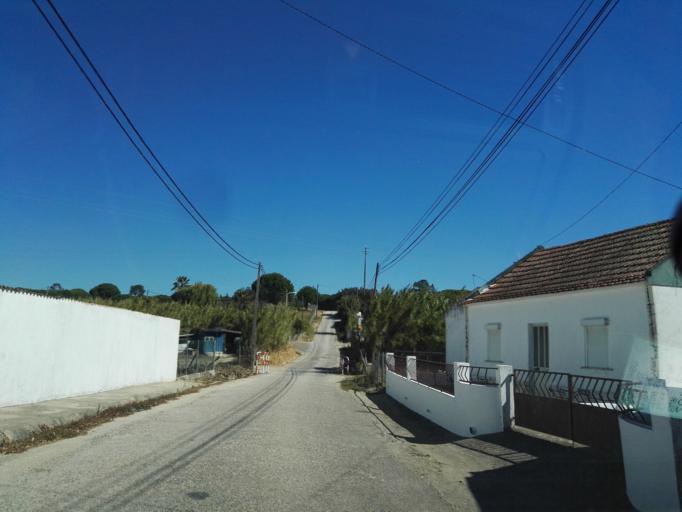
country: PT
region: Santarem
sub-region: Benavente
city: Poceirao
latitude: 38.8667
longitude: -8.7427
